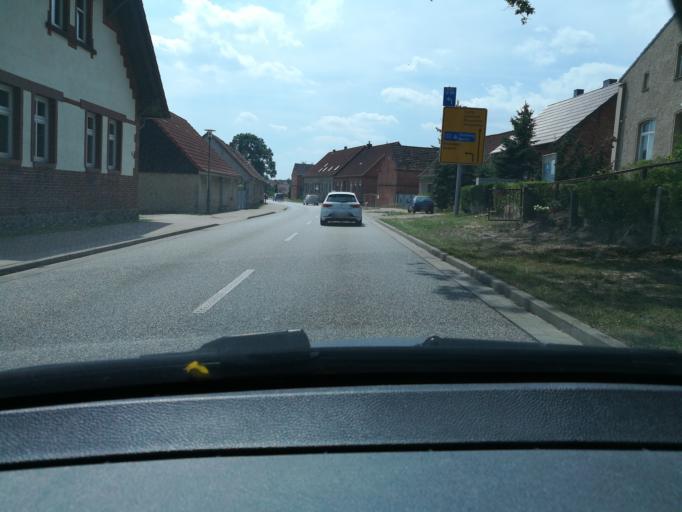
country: DE
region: Brandenburg
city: Wittstock
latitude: 53.0712
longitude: 12.4740
